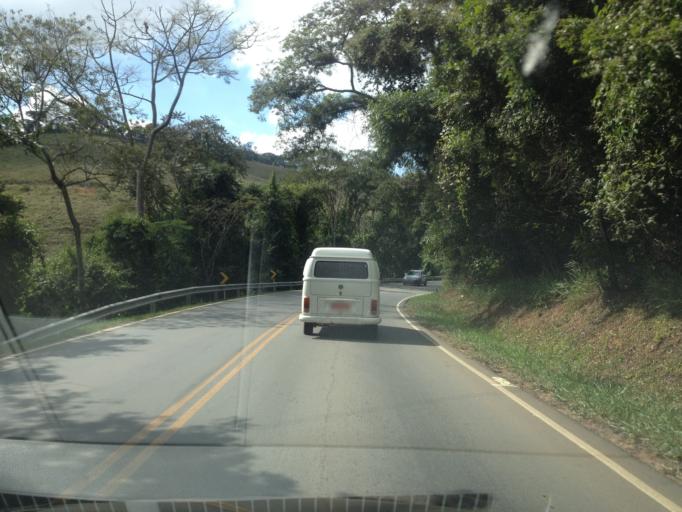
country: BR
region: Minas Gerais
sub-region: Itanhandu
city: Itanhandu
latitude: -22.2045
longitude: -44.9613
